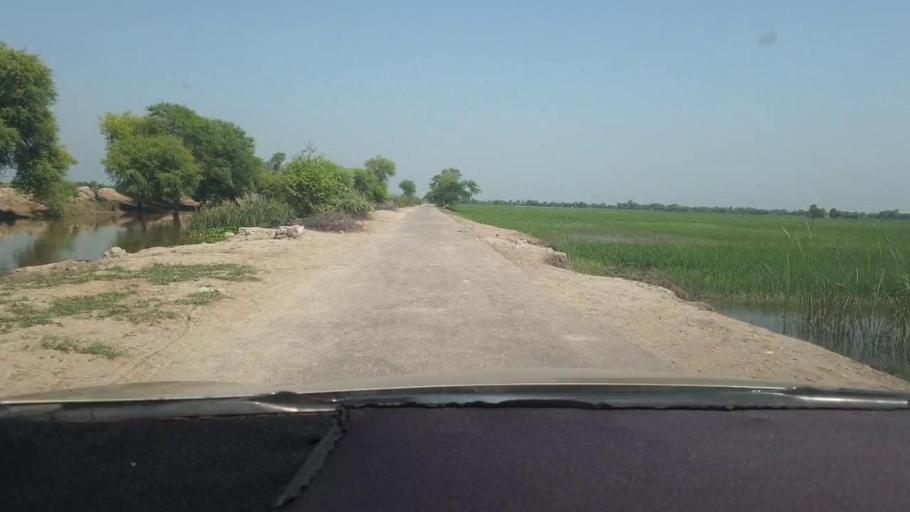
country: PK
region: Sindh
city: Miro Khan
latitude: 27.7070
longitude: 68.0685
